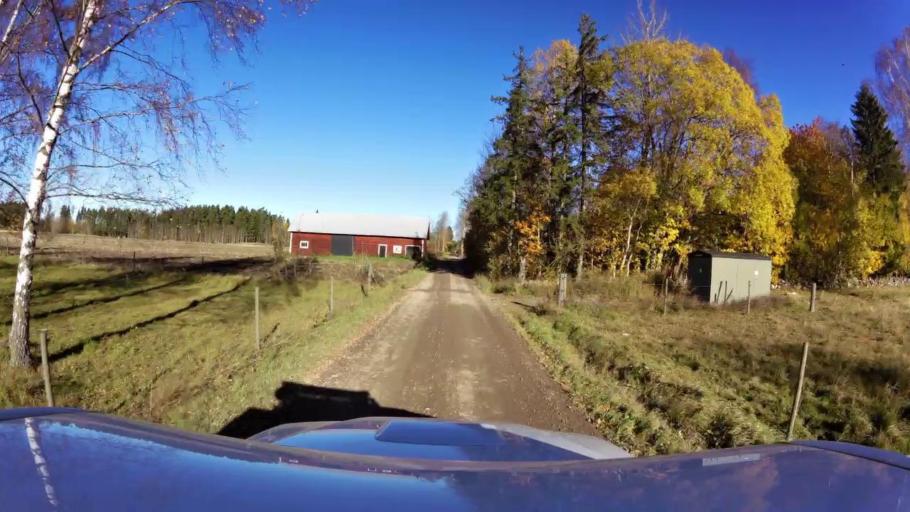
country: SE
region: OEstergoetland
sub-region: Linkopings Kommun
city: Ljungsbro
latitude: 58.5026
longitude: 15.3855
